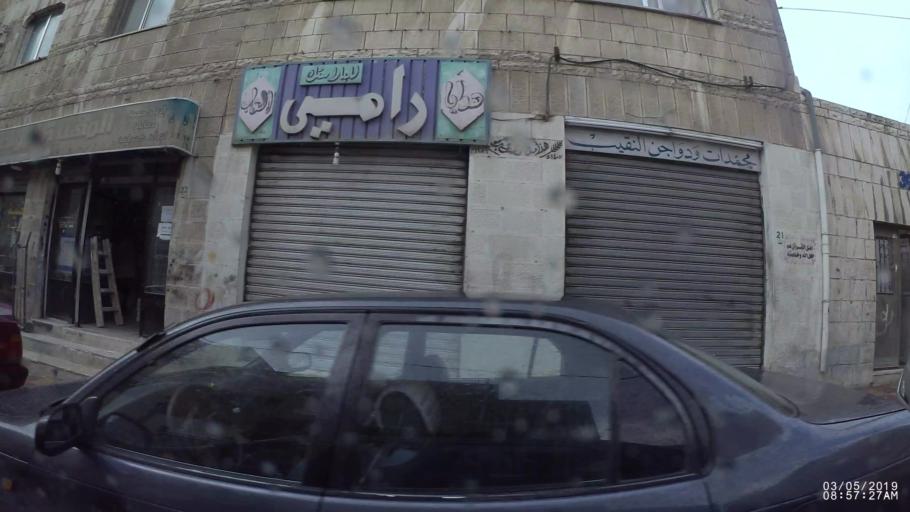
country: JO
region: Amman
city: Amman
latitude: 31.9591
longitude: 35.9379
